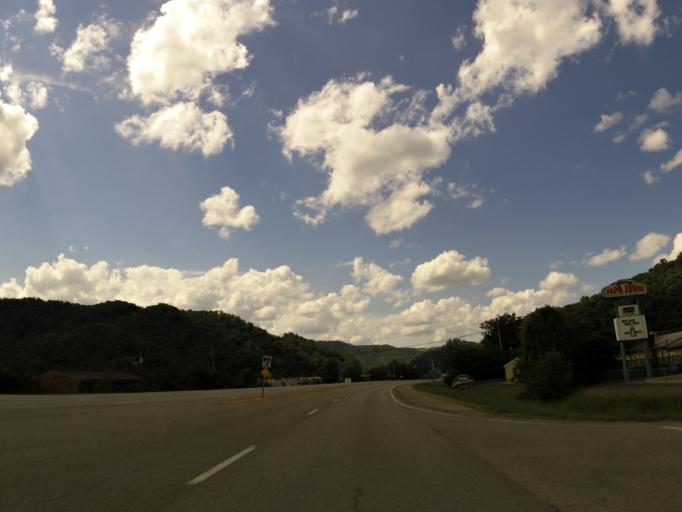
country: US
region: Kentucky
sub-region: Harlan County
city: Harlan
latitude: 36.8116
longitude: -83.3133
